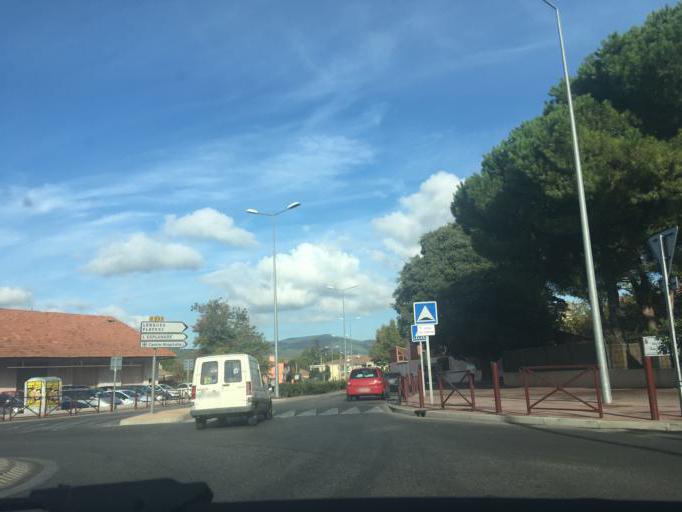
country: FR
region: Provence-Alpes-Cote d'Azur
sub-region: Departement du Var
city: Draguignan
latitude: 43.5333
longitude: 6.4640
